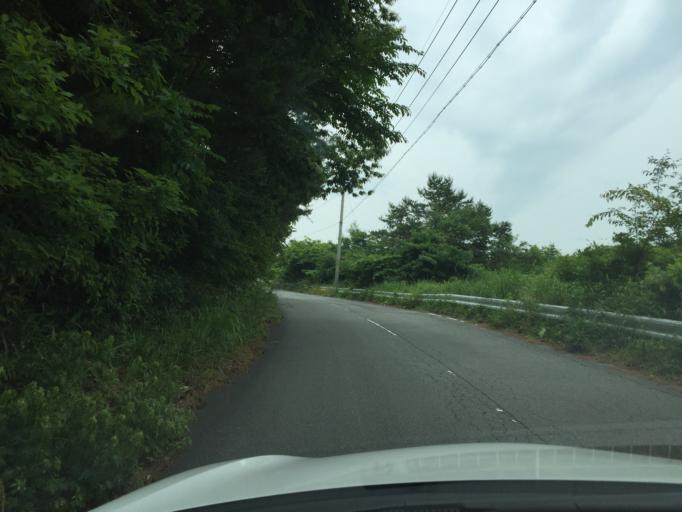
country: JP
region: Fukushima
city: Iwaki
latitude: 37.1550
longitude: 140.7009
